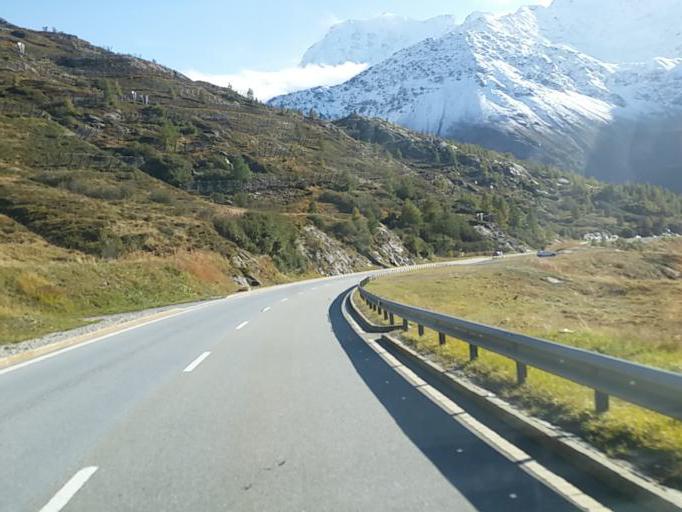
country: CH
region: Valais
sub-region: Brig District
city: Brig
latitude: 46.2398
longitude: 8.0216
